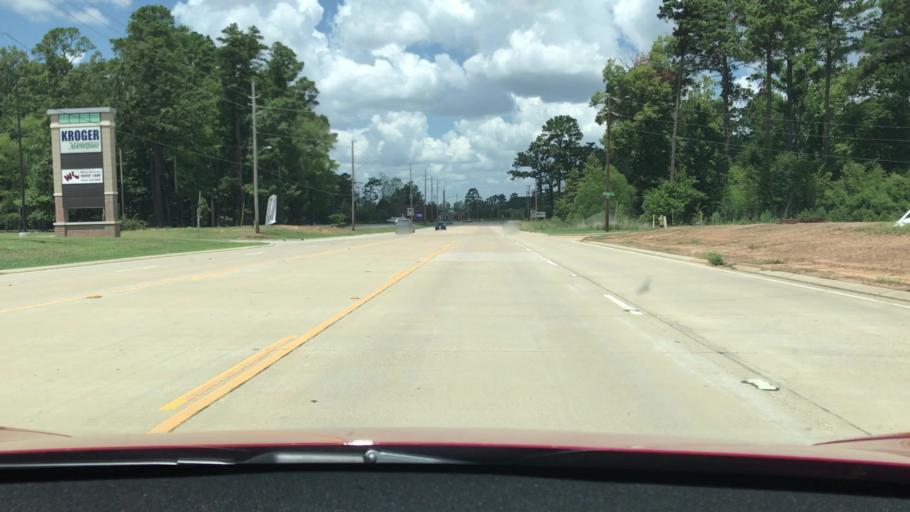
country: US
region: Louisiana
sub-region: Bossier Parish
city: Bossier City
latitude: 32.3973
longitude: -93.7298
